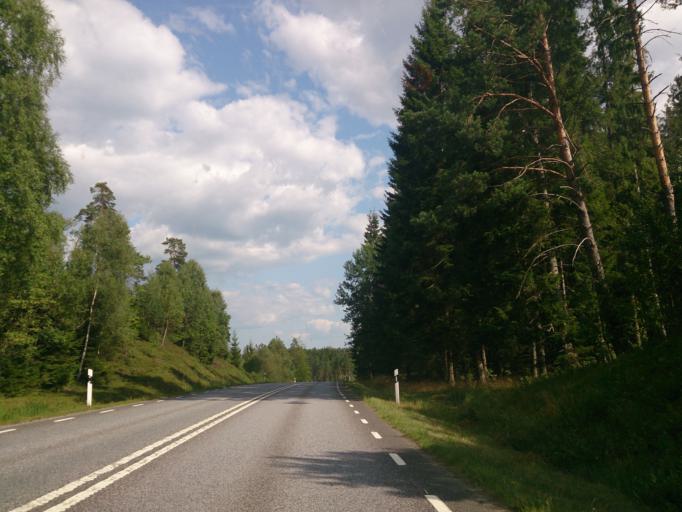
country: SE
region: Joenkoeping
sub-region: Gislaveds Kommun
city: Smalandsstenar
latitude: 57.1584
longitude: 13.4805
